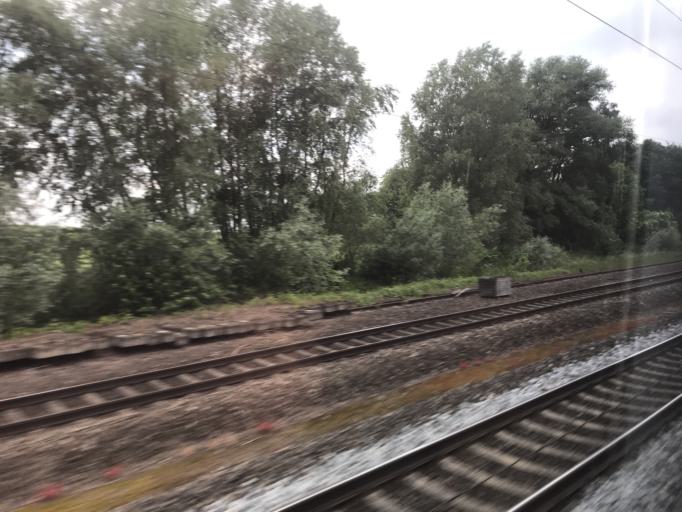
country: DE
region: Bavaria
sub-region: Swabia
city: Dinkelscherben
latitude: 48.3406
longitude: 10.5929
